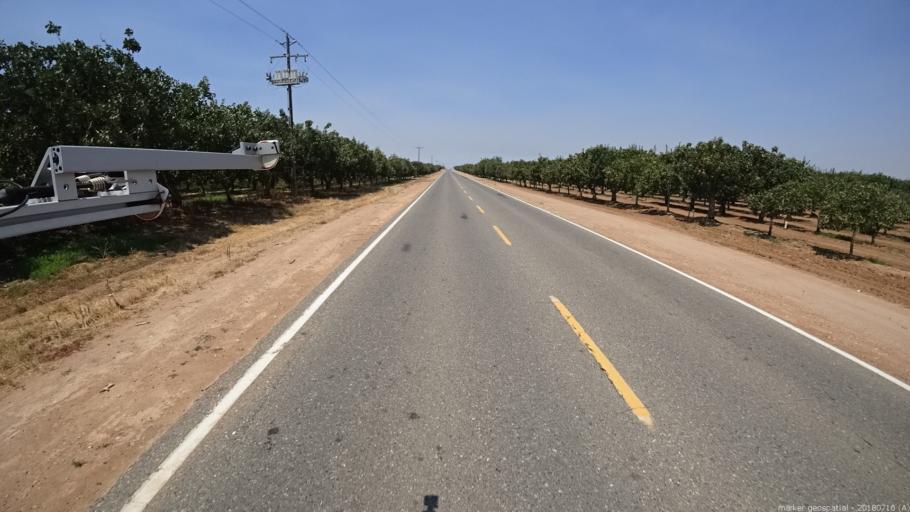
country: US
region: California
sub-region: Madera County
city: Madera Acres
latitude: 37.0543
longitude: -120.0485
